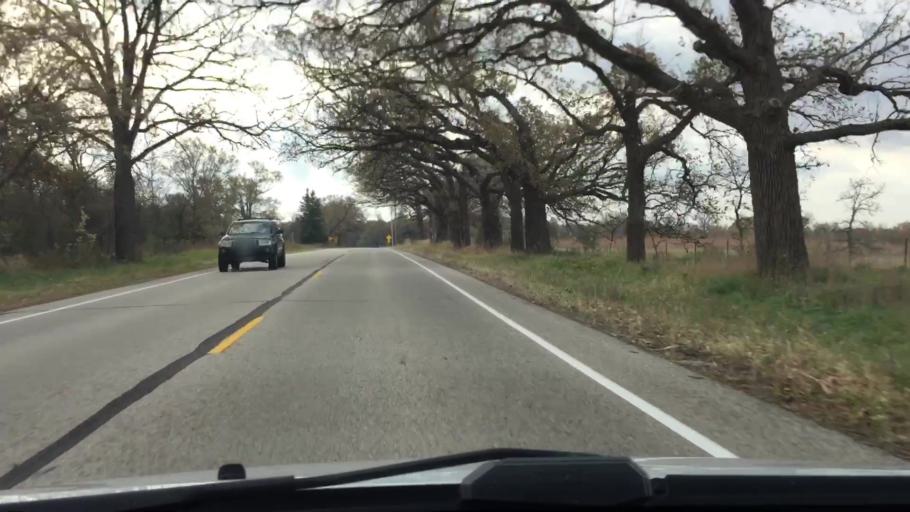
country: US
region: Wisconsin
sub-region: Waukesha County
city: Dousman
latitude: 42.9498
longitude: -88.4786
